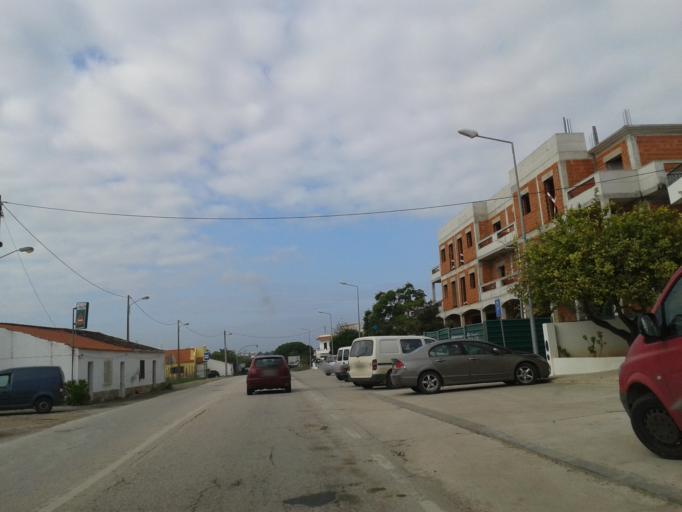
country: PT
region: Faro
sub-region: Vila Real de Santo Antonio
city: Monte Gordo
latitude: 37.1807
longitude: -7.5040
